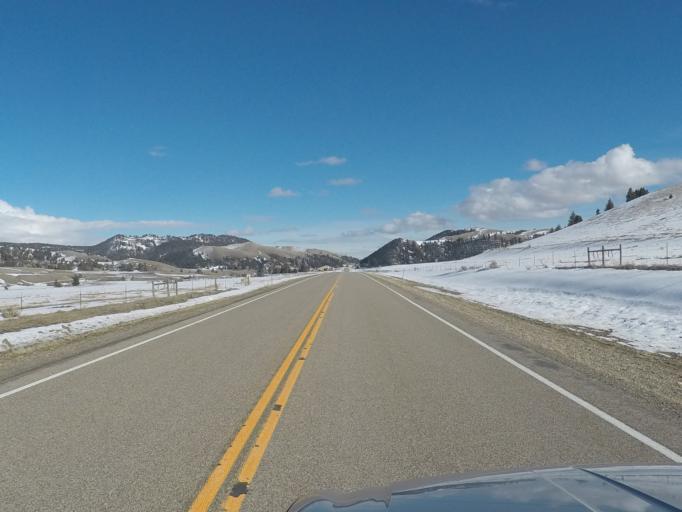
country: US
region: Montana
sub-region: Meagher County
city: White Sulphur Springs
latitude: 46.5709
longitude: -110.5408
